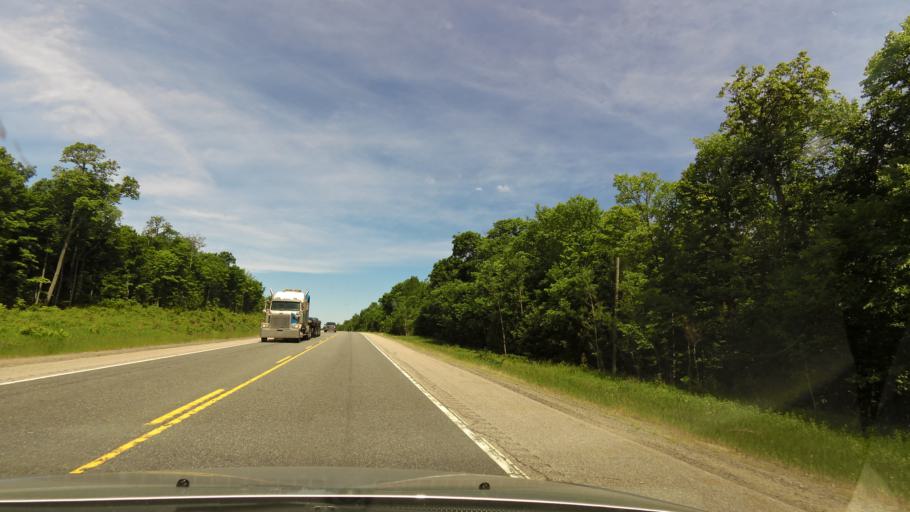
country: CA
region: Ontario
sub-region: Parry Sound District
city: Parry Sound
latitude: 45.4790
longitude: -80.1807
